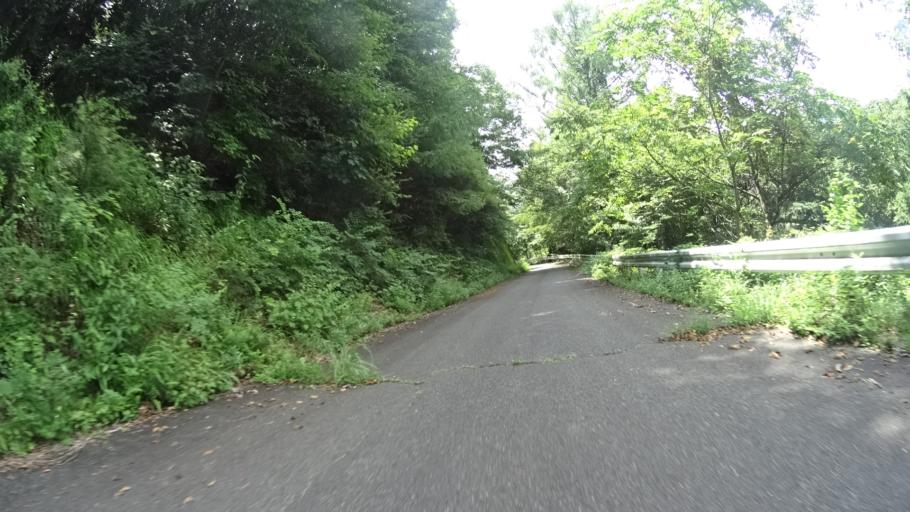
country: JP
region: Yamanashi
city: Nirasaki
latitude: 35.8818
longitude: 138.4955
